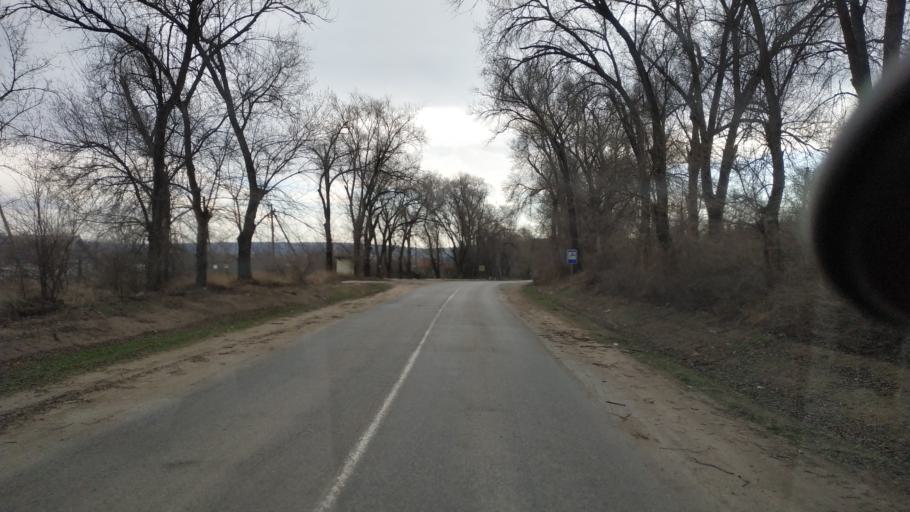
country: MD
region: Chisinau
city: Vadul lui Voda
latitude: 47.1223
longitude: 29.0638
